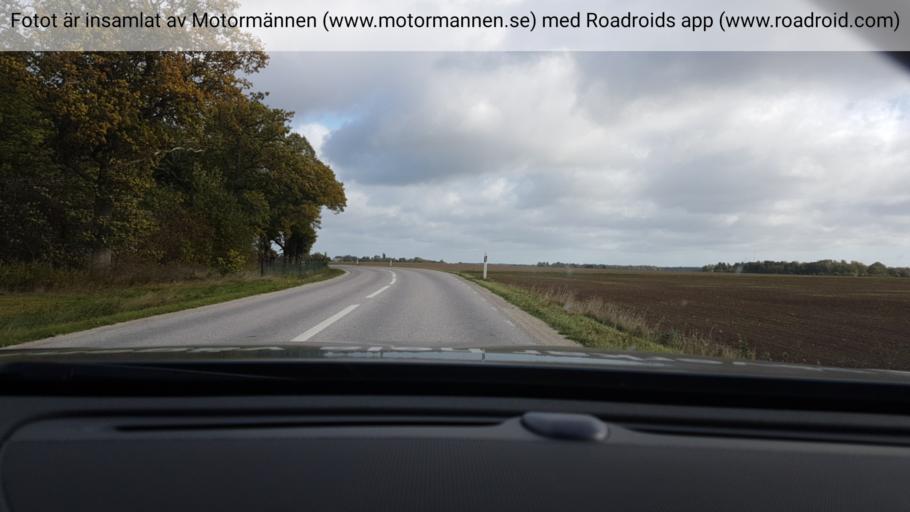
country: SE
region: Gotland
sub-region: Gotland
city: Visby
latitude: 57.6976
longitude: 18.5060
